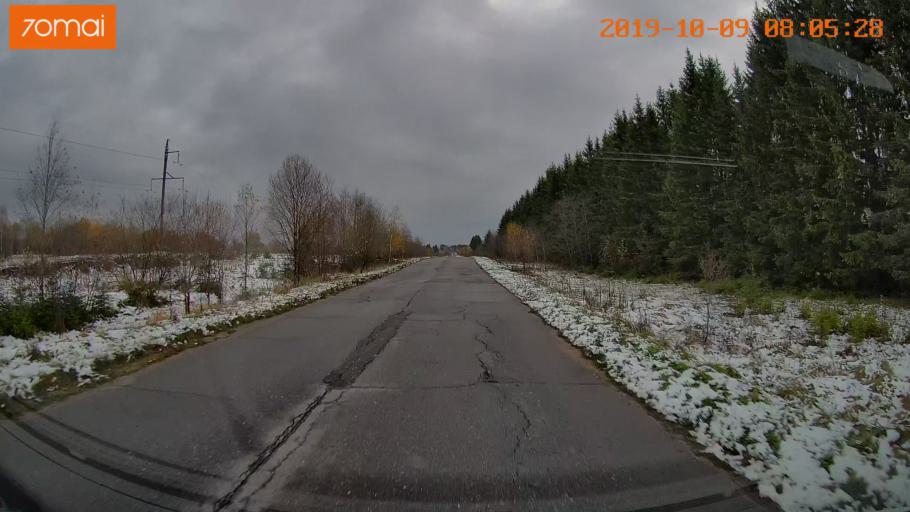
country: RU
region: Jaroslavl
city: Kukoboy
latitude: 58.6913
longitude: 40.0446
